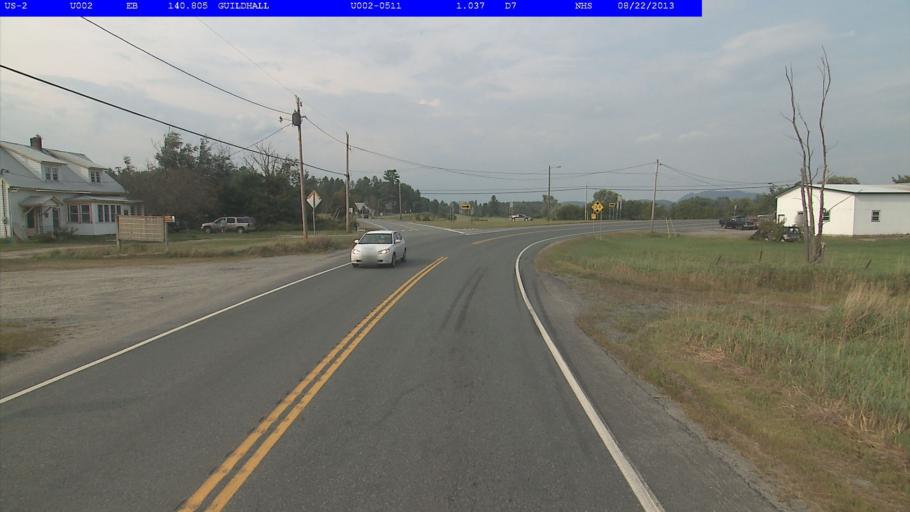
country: US
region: New Hampshire
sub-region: Coos County
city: Lancaster
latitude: 44.4953
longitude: -71.5964
